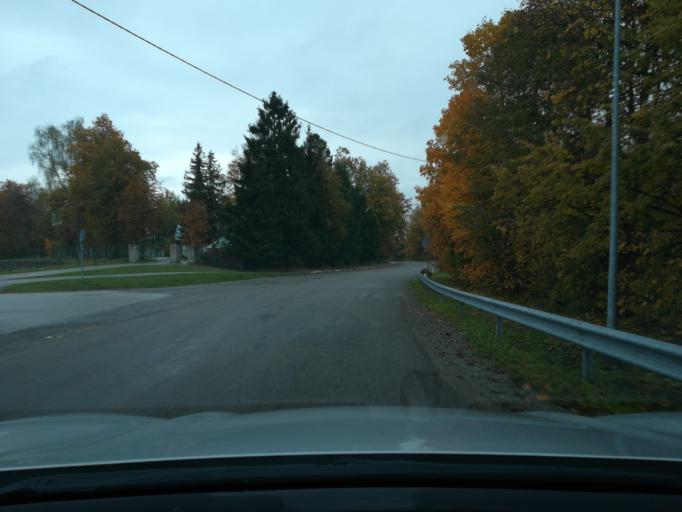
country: EE
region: Ida-Virumaa
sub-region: Johvi vald
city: Johvi
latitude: 59.2005
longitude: 27.5354
